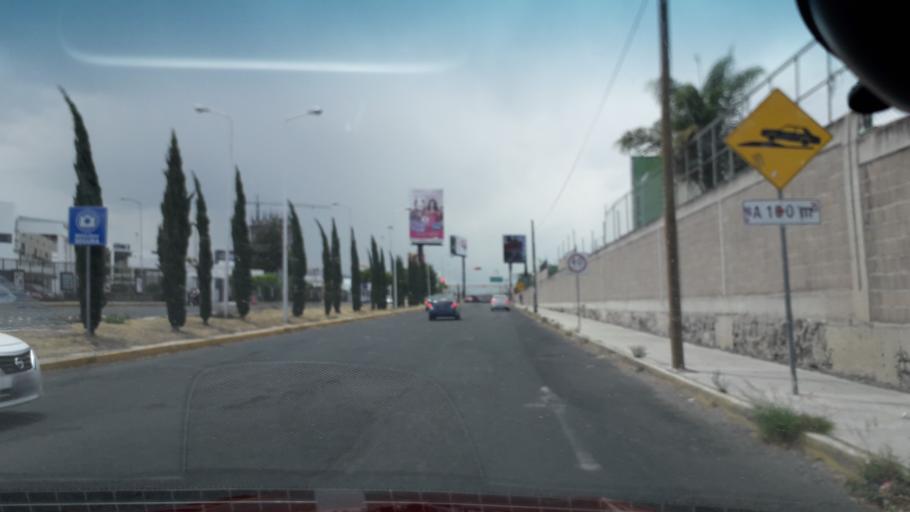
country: MX
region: Puebla
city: Puebla
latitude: 19.0216
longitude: -98.2397
